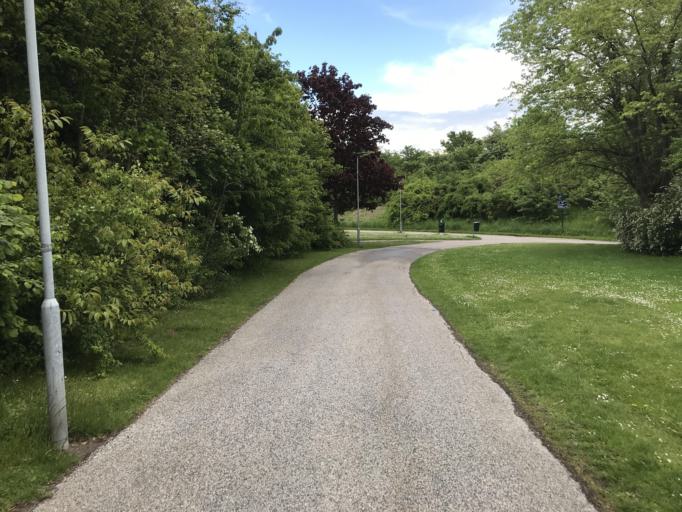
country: SE
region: Skane
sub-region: Malmo
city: Malmoe
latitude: 55.5659
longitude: 13.0311
